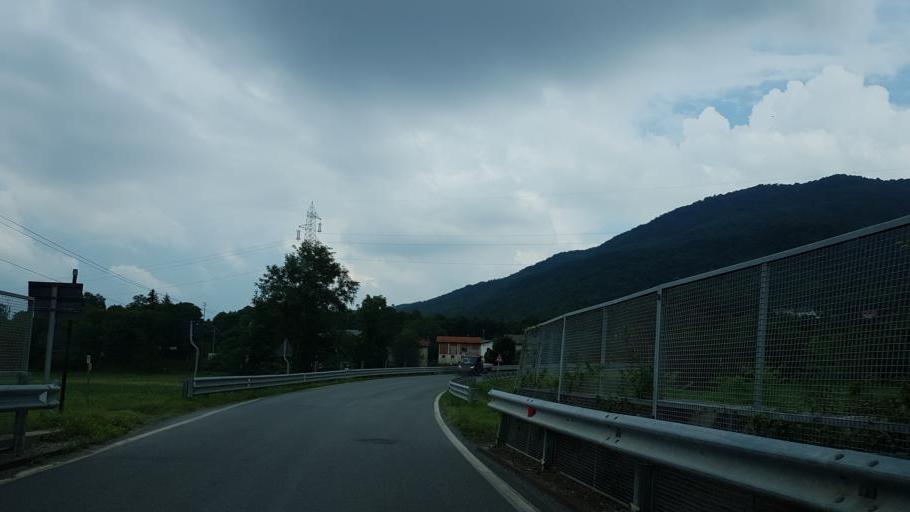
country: IT
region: Piedmont
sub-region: Provincia di Cuneo
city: Gaiola
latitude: 44.3364
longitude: 7.4173
